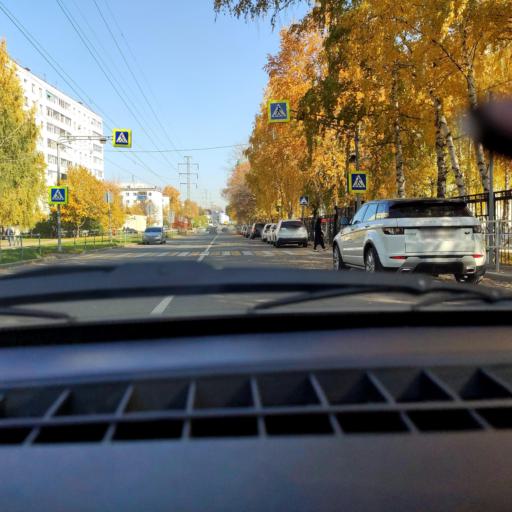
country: RU
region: Bashkortostan
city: Ufa
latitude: 54.7672
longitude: 56.0246
